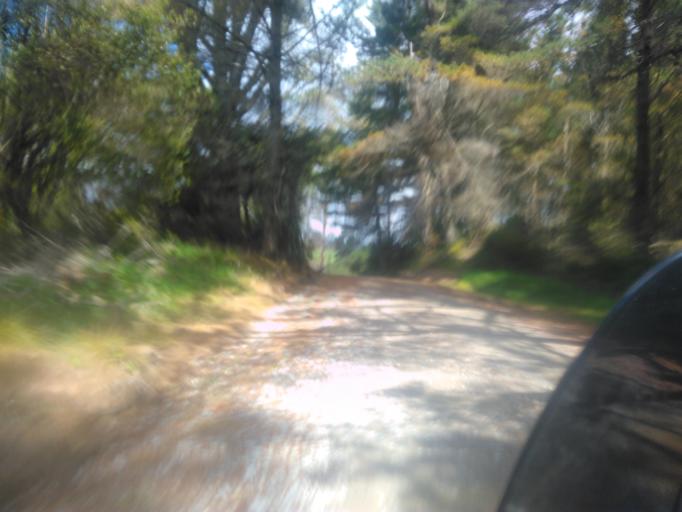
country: NZ
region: Hawke's Bay
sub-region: Wairoa District
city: Wairoa
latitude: -38.7779
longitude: 177.6130
